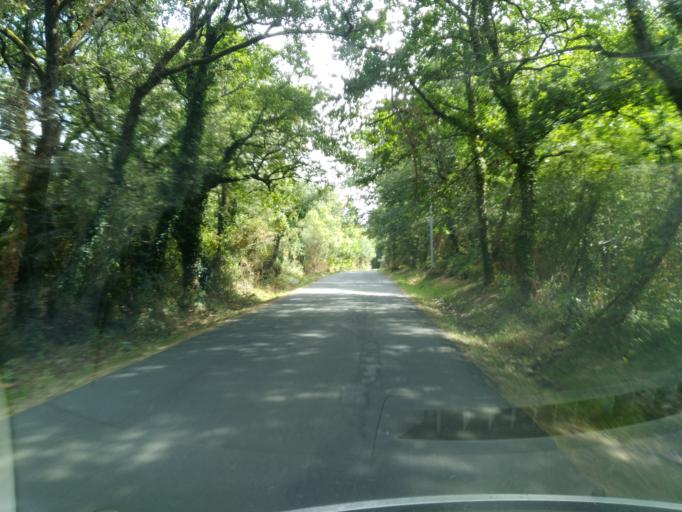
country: FR
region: Poitou-Charentes
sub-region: Departement de la Charente-Maritime
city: Chaillevette
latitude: 45.7162
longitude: -1.0767
